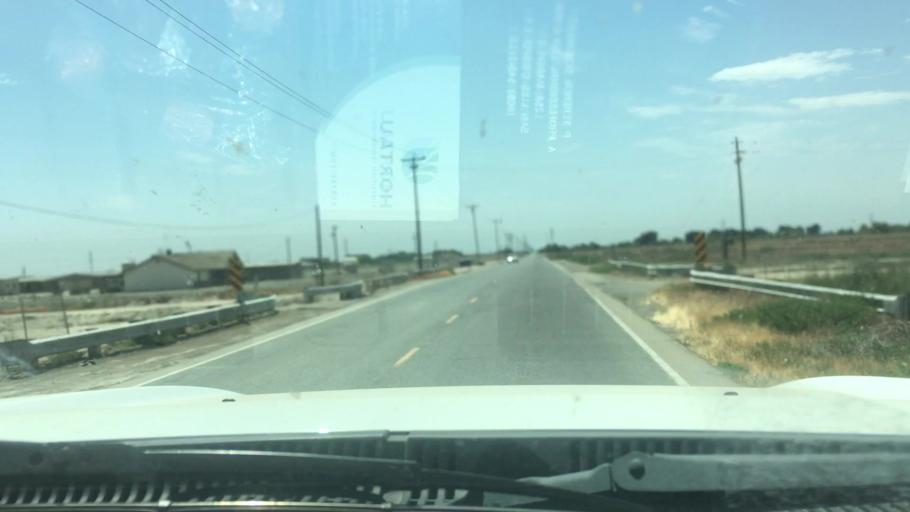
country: US
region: California
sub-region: Kings County
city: Corcoran
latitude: 36.0508
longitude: -119.4869
